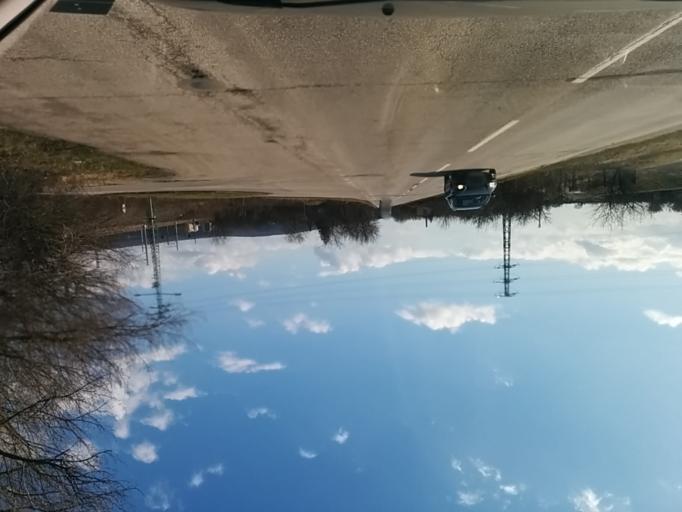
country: SK
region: Trenciansky
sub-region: Okres Nove Mesto nad Vahom
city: Nove Mesto nad Vahom
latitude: 48.7720
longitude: 17.8499
